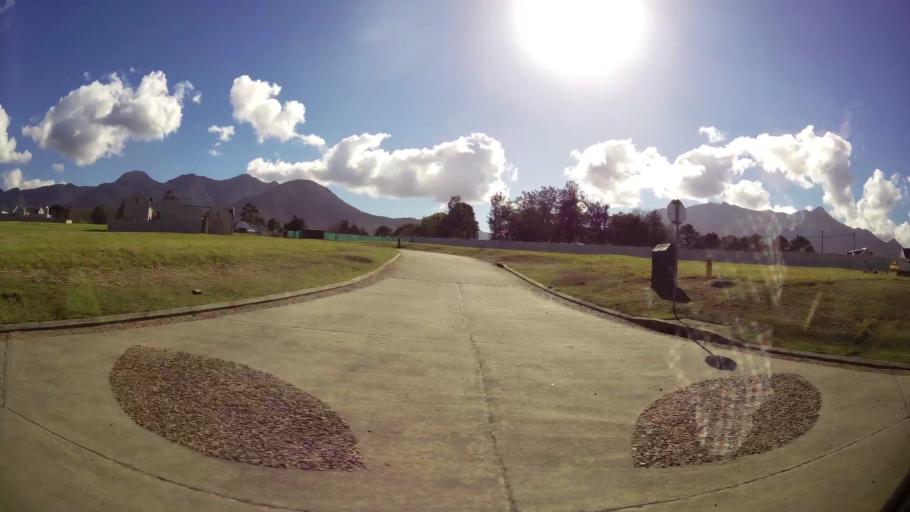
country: ZA
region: Western Cape
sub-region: Eden District Municipality
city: George
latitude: -33.9422
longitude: 22.4056
